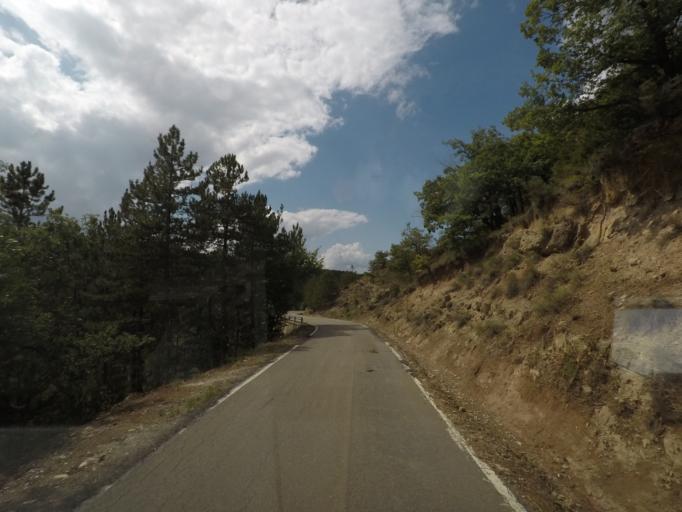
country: ES
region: Aragon
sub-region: Provincia de Huesca
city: Fiscal
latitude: 42.4061
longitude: -0.1428
